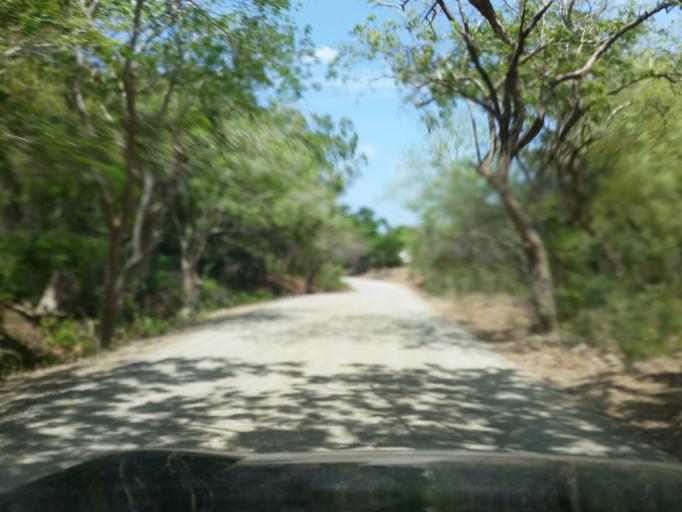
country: NI
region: Rivas
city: Tola
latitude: 11.4911
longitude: -86.0945
